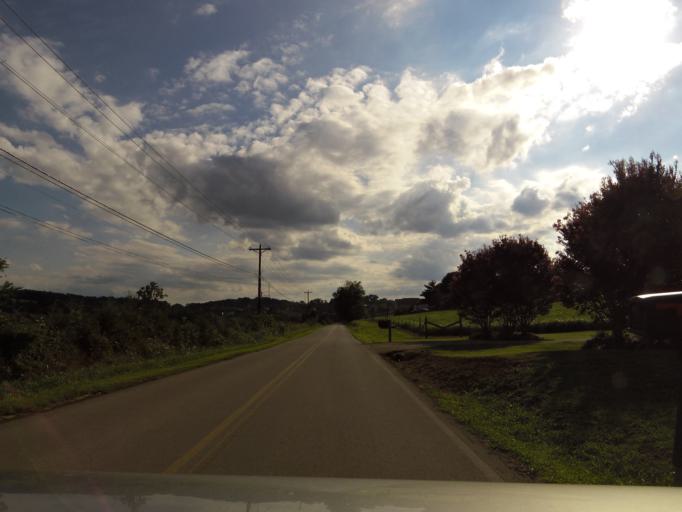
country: US
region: Tennessee
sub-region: Loudon County
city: Greenback
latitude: 35.6591
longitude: -84.0983
